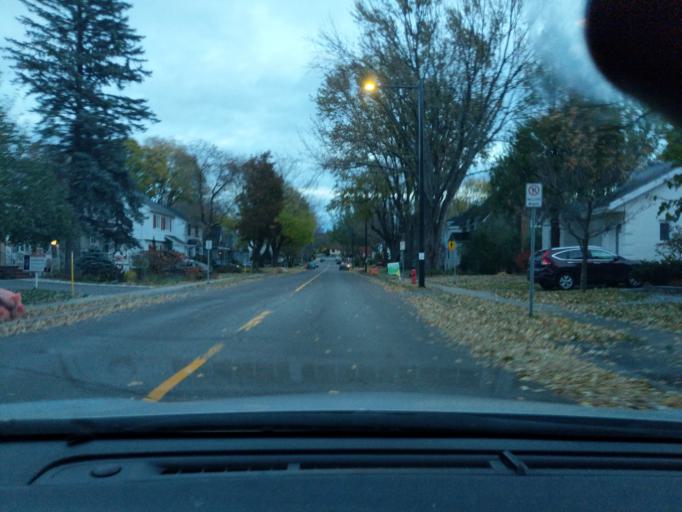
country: CA
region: Quebec
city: Quebec
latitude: 46.7900
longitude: -71.2512
